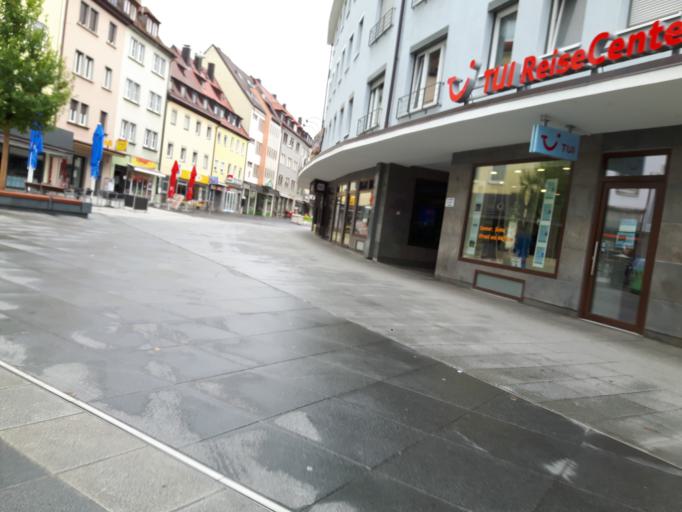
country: DE
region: Bavaria
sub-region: Regierungsbezirk Unterfranken
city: Wuerzburg
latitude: 49.7954
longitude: 9.9331
